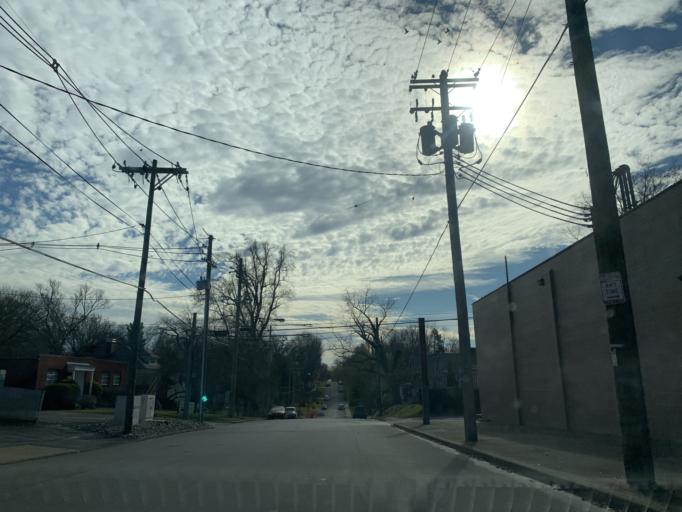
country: US
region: Kentucky
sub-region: Jefferson County
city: Indian Hills
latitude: 38.2535
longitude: -85.6999
